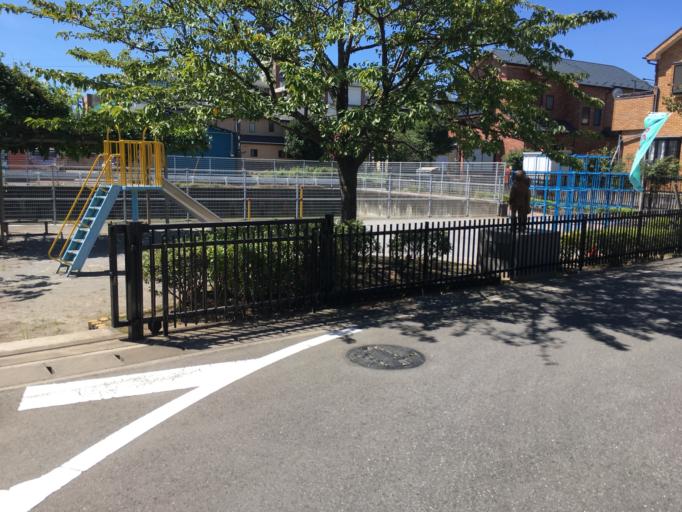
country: JP
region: Chiba
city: Matsudo
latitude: 35.8060
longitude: 139.8944
